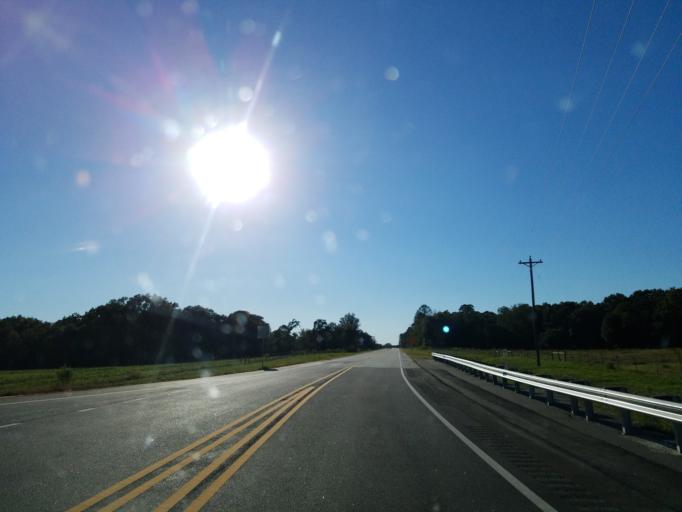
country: US
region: Georgia
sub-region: Lee County
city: Leesburg
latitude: 31.7500
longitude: -84.1590
